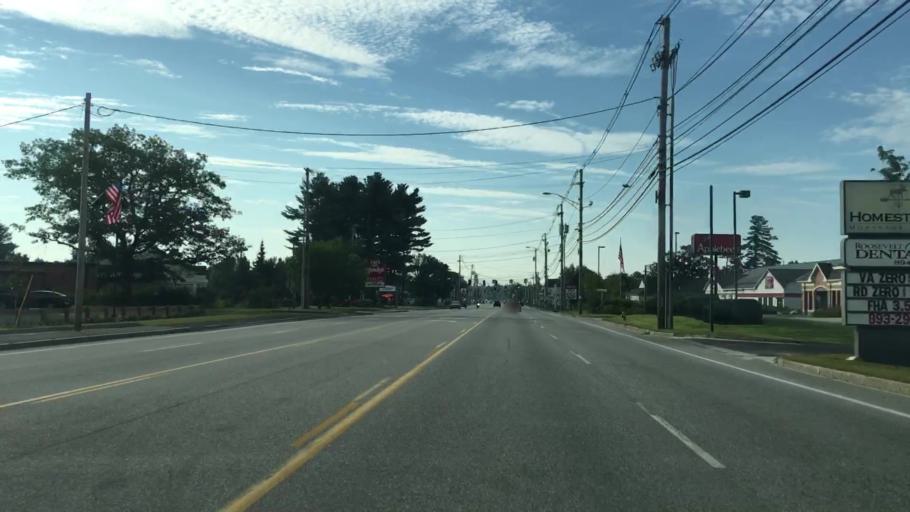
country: US
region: Maine
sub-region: Cumberland County
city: North Windham
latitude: 43.8426
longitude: -70.4456
